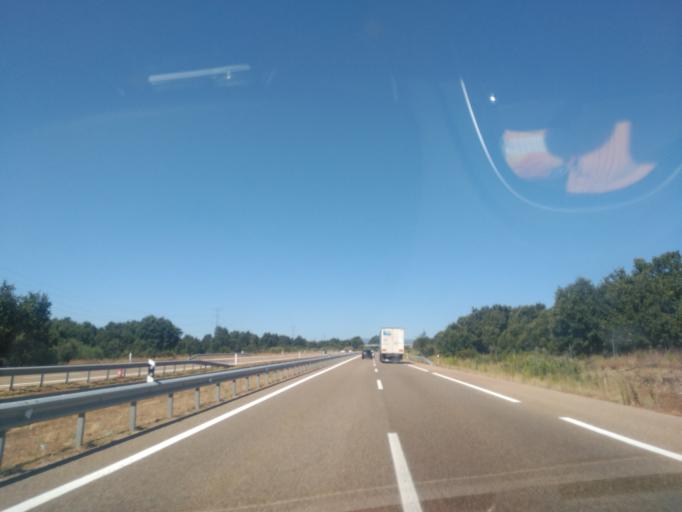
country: ES
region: Castille and Leon
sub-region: Provincia de Zamora
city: Asturianos
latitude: 42.0392
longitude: -6.4524
